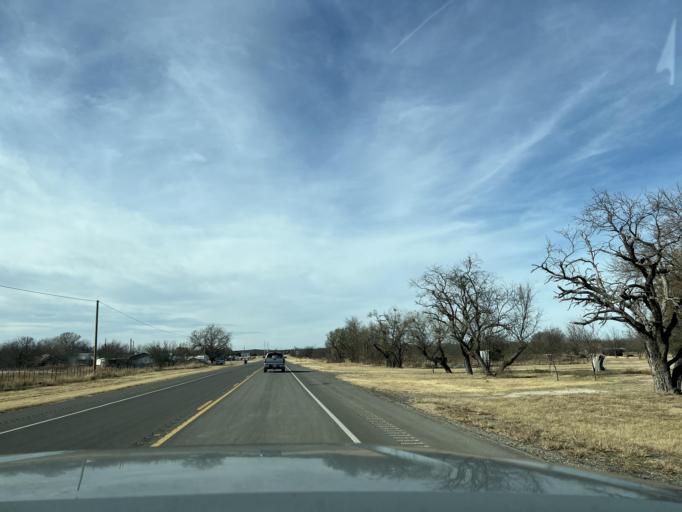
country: US
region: Texas
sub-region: Shackelford County
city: Albany
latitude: 32.7169
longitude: -99.2853
